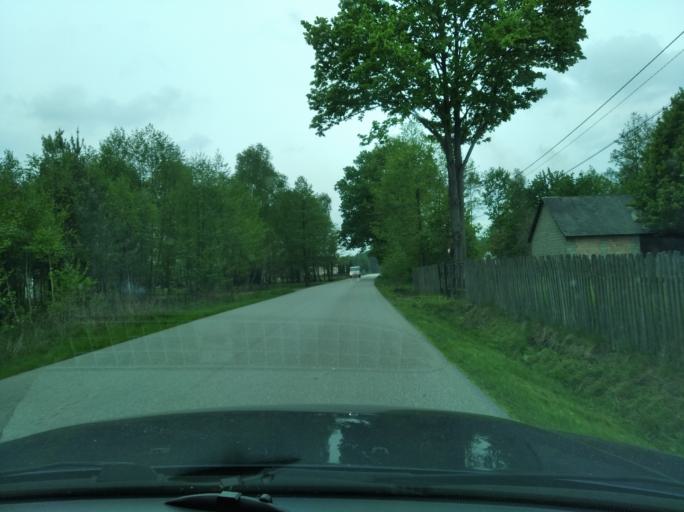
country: PL
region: Subcarpathian Voivodeship
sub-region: Powiat kolbuszowski
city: Kolbuszowa
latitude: 50.1964
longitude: 21.7839
